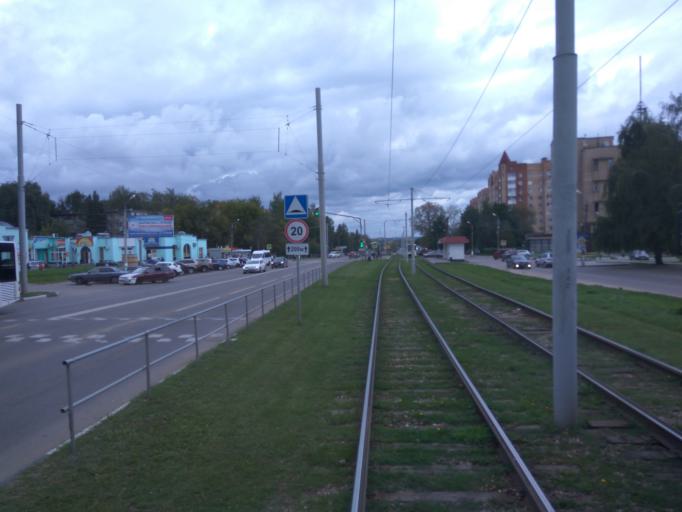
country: RU
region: Moskovskaya
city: Kolomna
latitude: 55.0829
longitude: 38.7634
